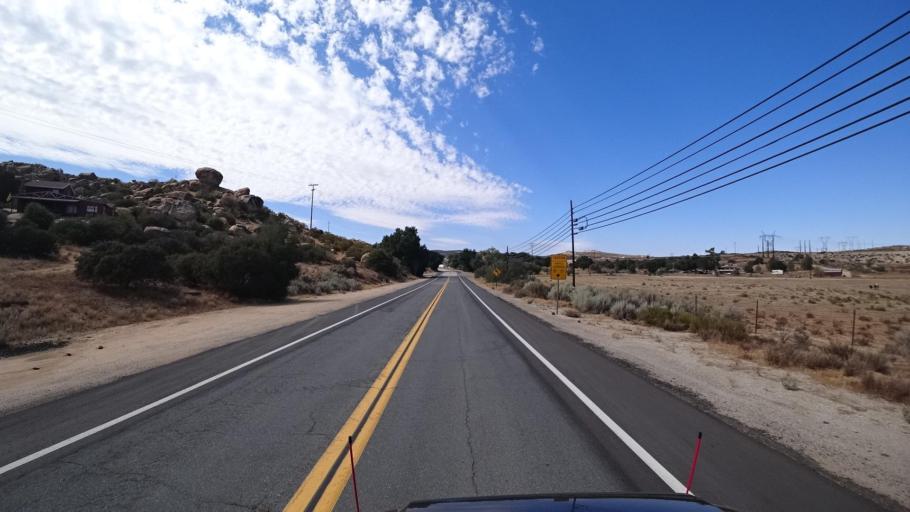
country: MX
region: Baja California
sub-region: Tecate
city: Cereso del Hongo
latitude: 32.6626
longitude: -116.2589
